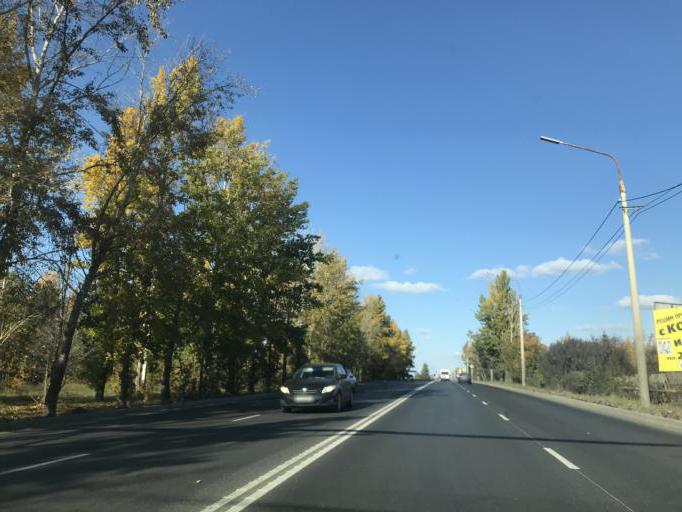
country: RU
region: Chelyabinsk
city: Roshchino
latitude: 55.2382
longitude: 61.3179
